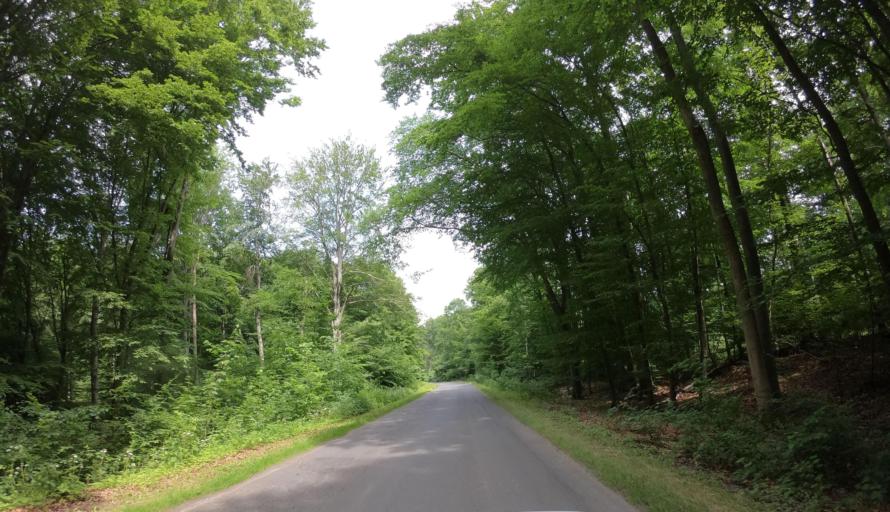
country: PL
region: West Pomeranian Voivodeship
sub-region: Powiat pyrzycki
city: Kozielice
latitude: 53.0757
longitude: 14.8239
